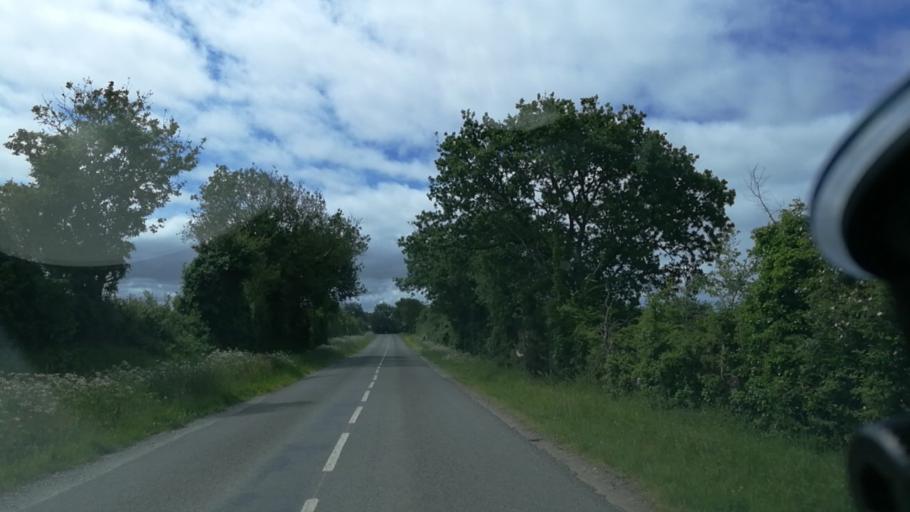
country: FR
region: Brittany
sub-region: Departement du Morbihan
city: Penestin
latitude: 47.4696
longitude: -2.4314
